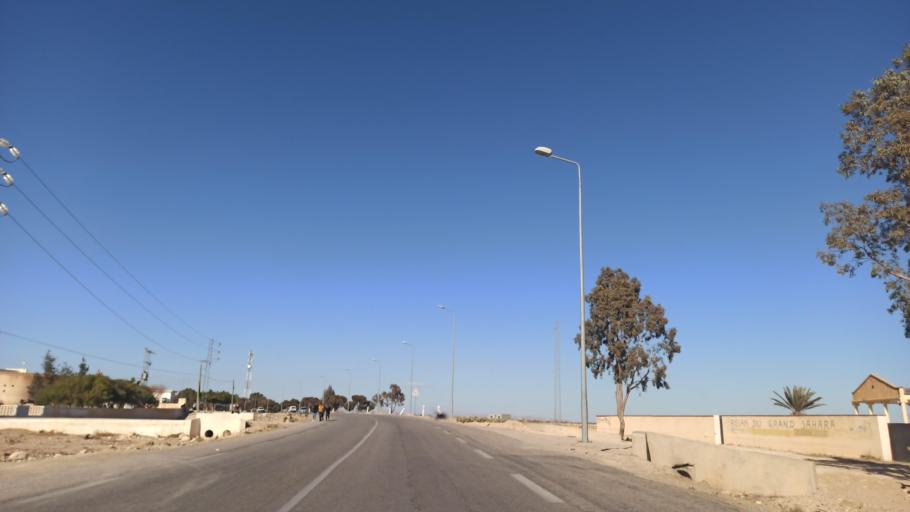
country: TN
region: Sidi Bu Zayd
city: Jilma
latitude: 35.2879
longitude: 9.4188
